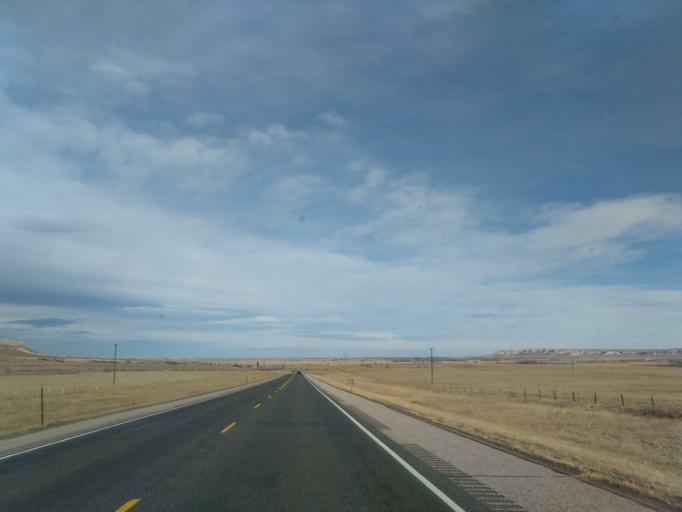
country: US
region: Wyoming
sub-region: Goshen County
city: Torrington
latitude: 41.6215
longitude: -104.2489
